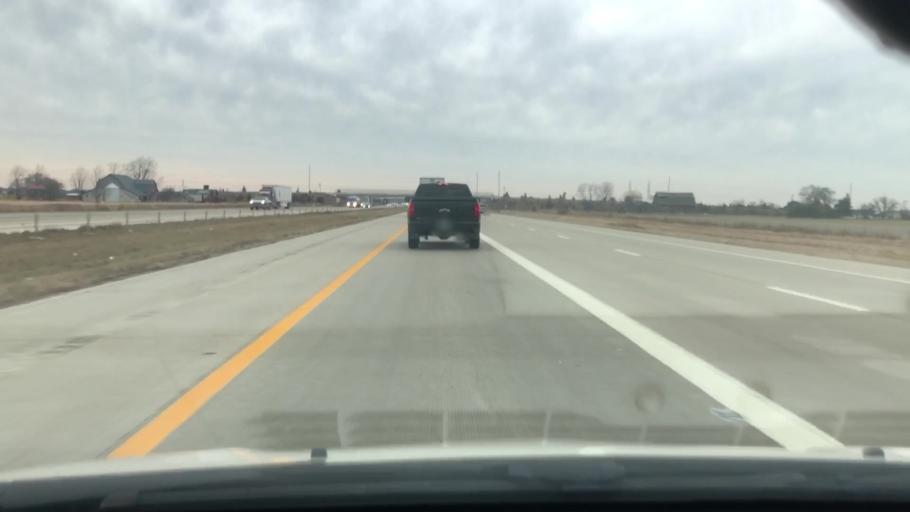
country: US
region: Ohio
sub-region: Wood County
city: Perrysburg
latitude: 41.5179
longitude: -83.6218
